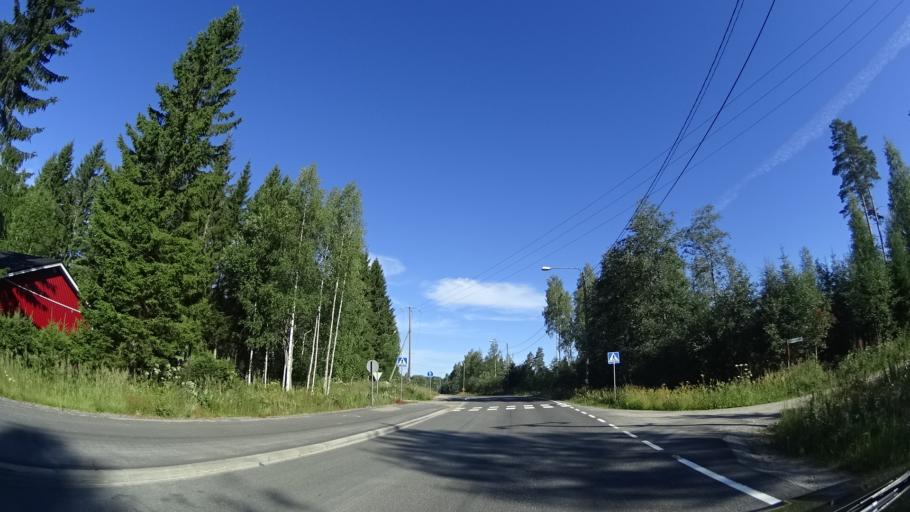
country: FI
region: Central Finland
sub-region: Jyvaeskylae
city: Petaejaevesi
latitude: 62.2717
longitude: 25.3393
